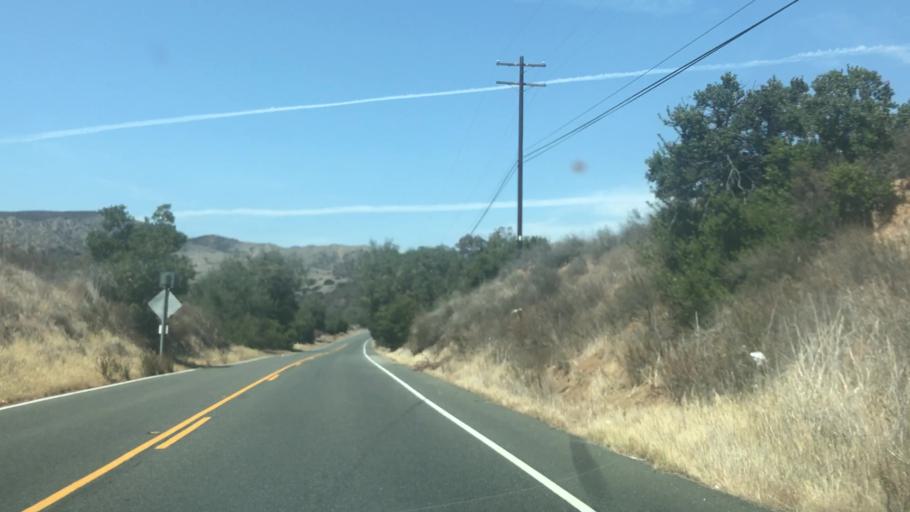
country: US
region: California
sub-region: Orange County
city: Coto De Caza
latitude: 33.5657
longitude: -117.5453
